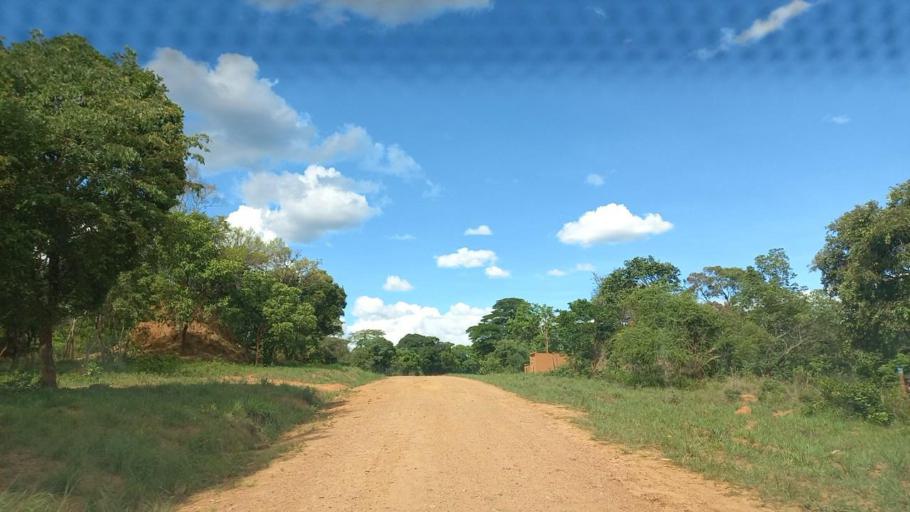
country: ZM
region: North-Western
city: Mwinilunga
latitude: -12.1180
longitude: 24.2785
